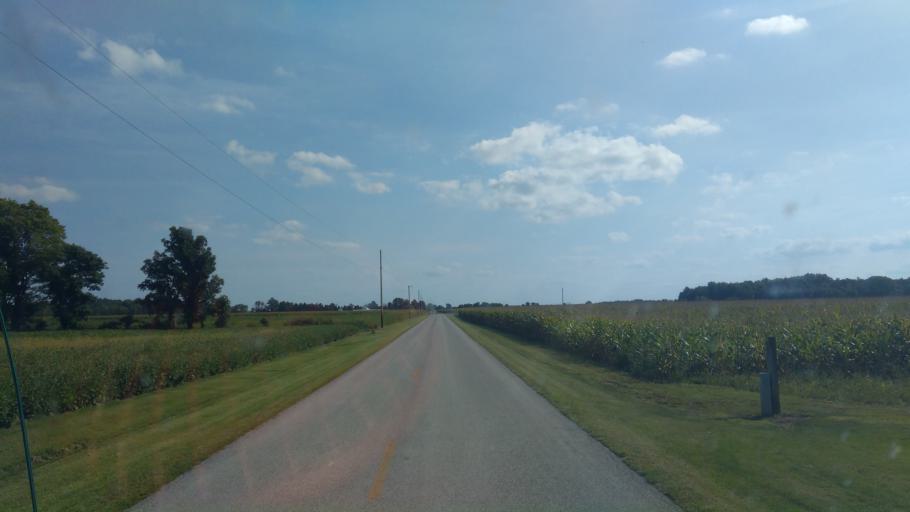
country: US
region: Ohio
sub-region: Hardin County
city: Forest
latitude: 40.7043
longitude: -83.5144
